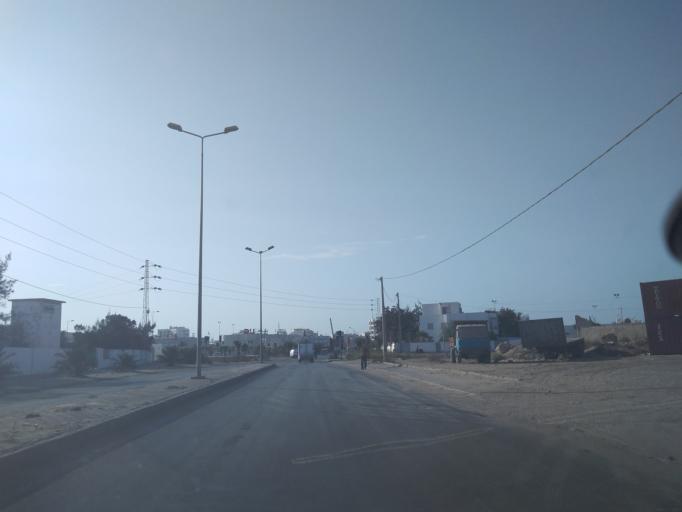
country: TN
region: Safaqis
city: Sfax
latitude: 34.7261
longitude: 10.7558
